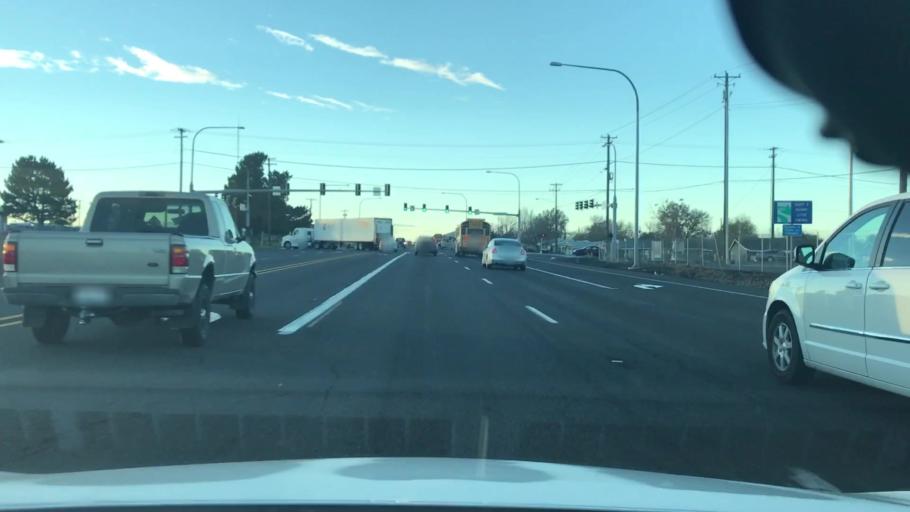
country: US
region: Washington
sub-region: Grant County
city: Moses Lake
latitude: 47.1320
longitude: -119.2569
